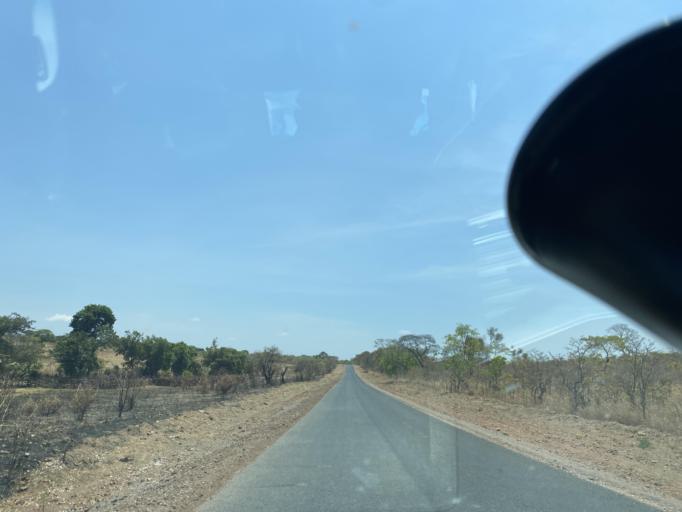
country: ZM
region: Lusaka
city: Kafue
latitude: -15.8394
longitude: 28.4072
